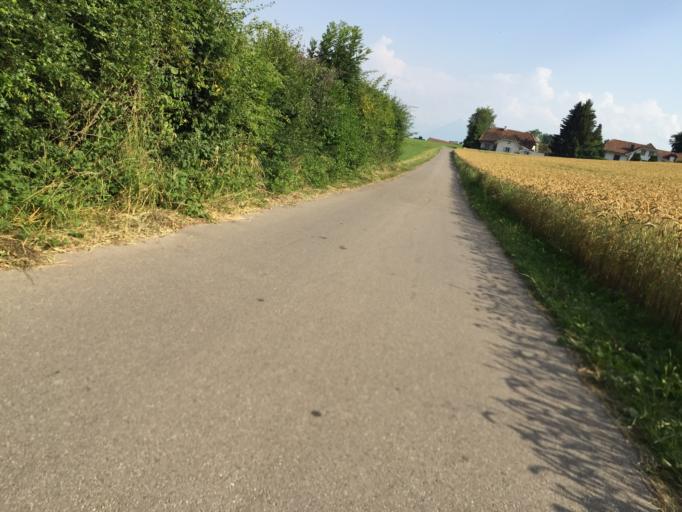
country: CH
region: Bern
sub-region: Bern-Mittelland District
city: Rubigen
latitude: 46.9216
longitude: 7.5216
